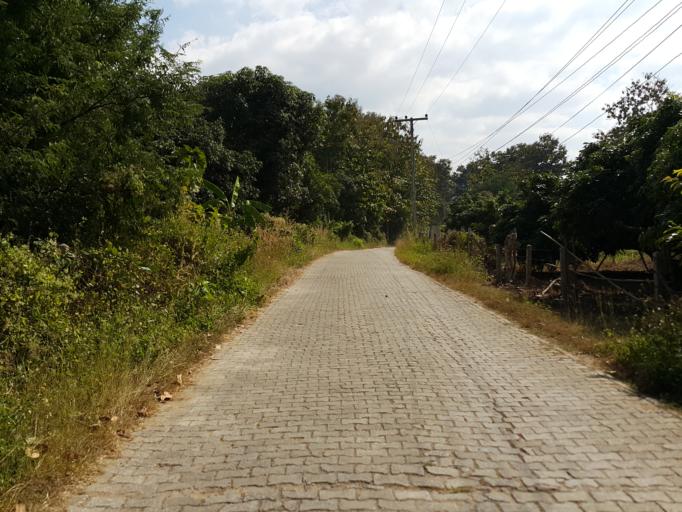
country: TH
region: Chiang Mai
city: Mae On
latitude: 18.7122
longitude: 99.2017
